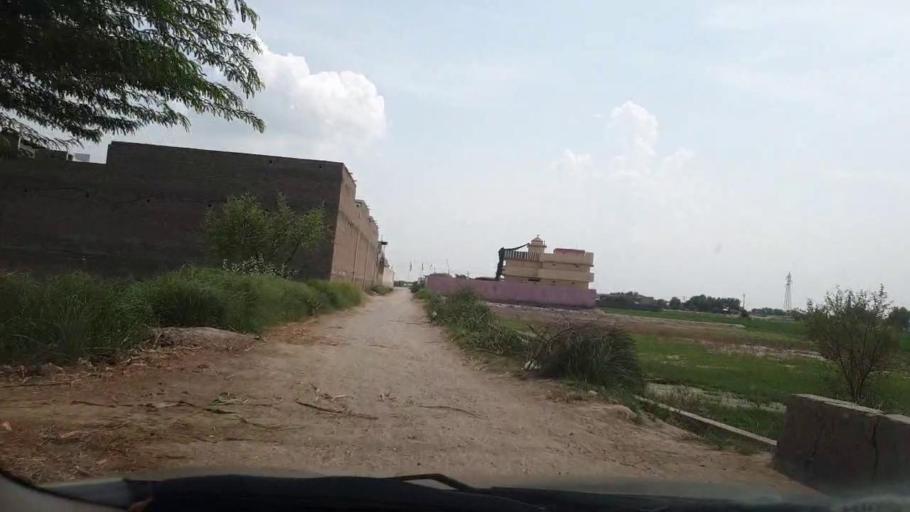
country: PK
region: Sindh
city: Larkana
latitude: 27.5768
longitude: 68.1644
